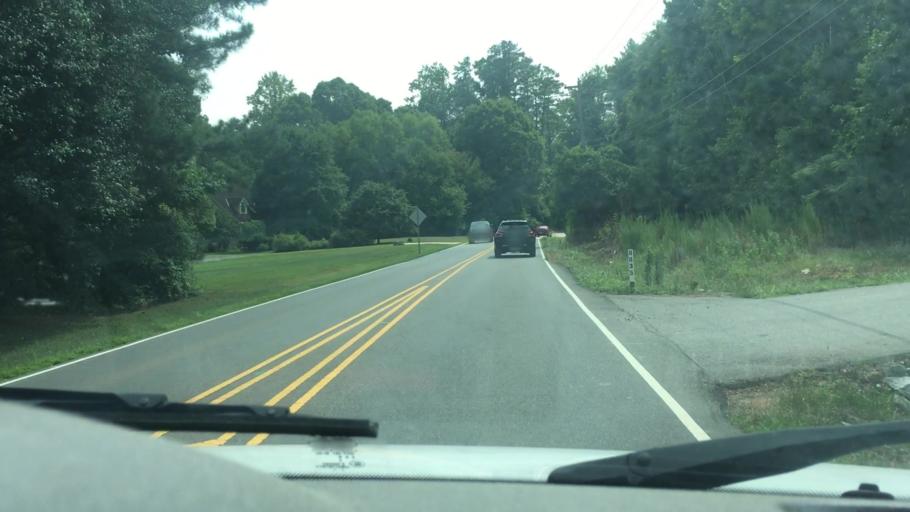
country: US
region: North Carolina
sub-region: Mecklenburg County
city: Huntersville
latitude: 35.4049
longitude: -80.8781
